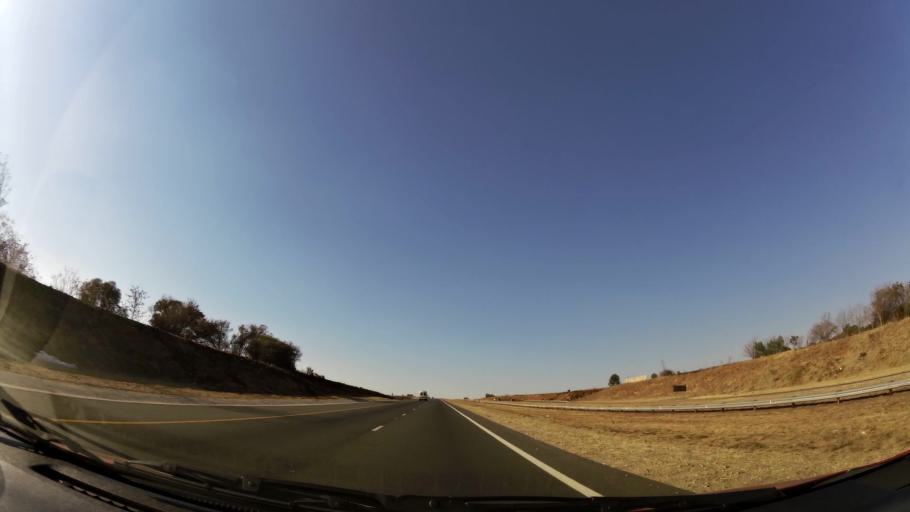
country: ZA
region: Gauteng
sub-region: West Rand District Municipality
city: Muldersdriseloop
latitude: -25.9967
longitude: 27.9077
